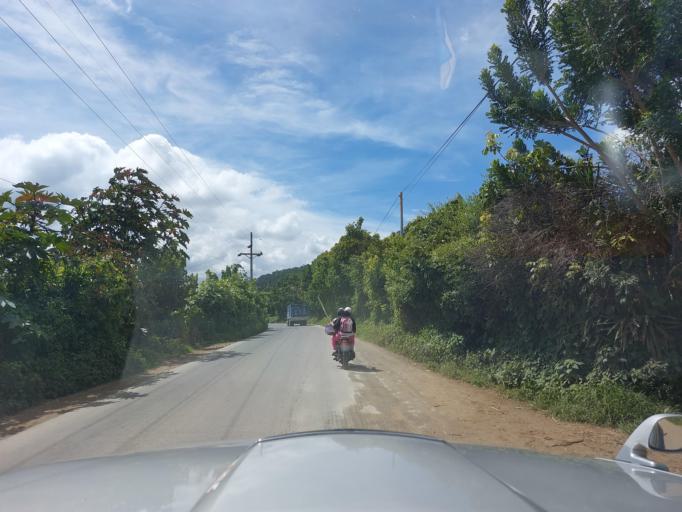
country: GT
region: Chimaltenango
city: San Andres Itzapa
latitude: 14.6187
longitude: -90.8332
